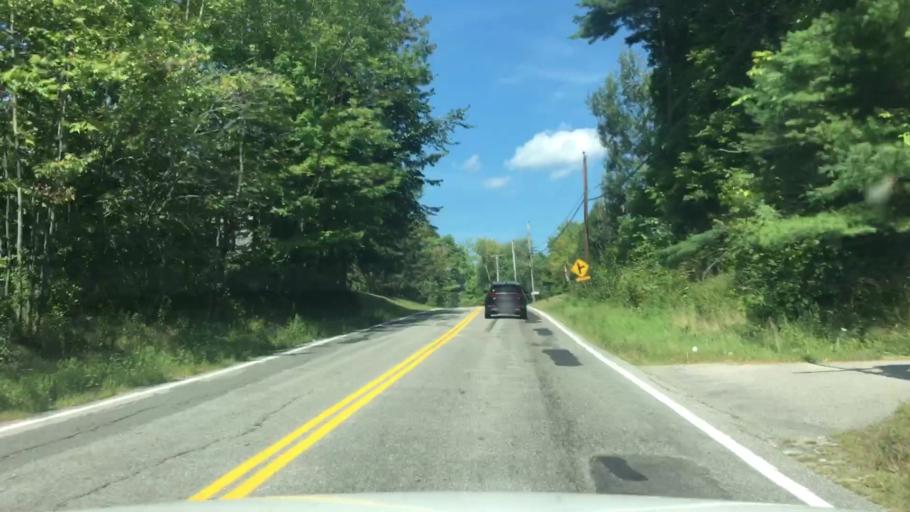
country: US
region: Maine
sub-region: Cumberland County
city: Falmouth
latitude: 43.7432
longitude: -70.2978
